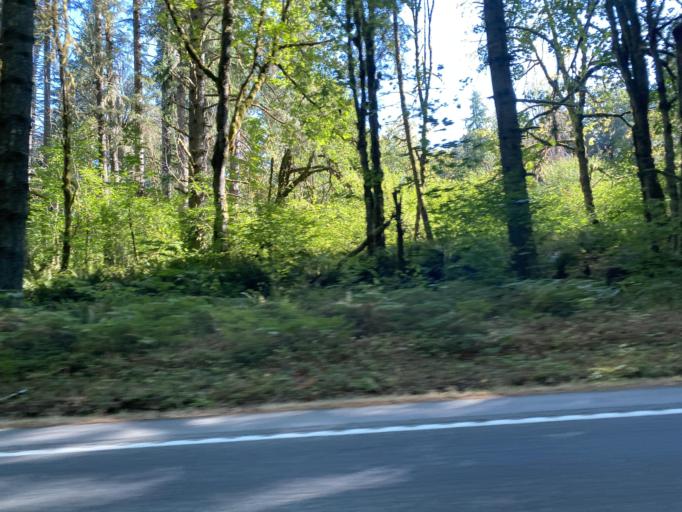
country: US
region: Washington
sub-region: Thurston County
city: Rainier
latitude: 46.9286
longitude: -122.7530
